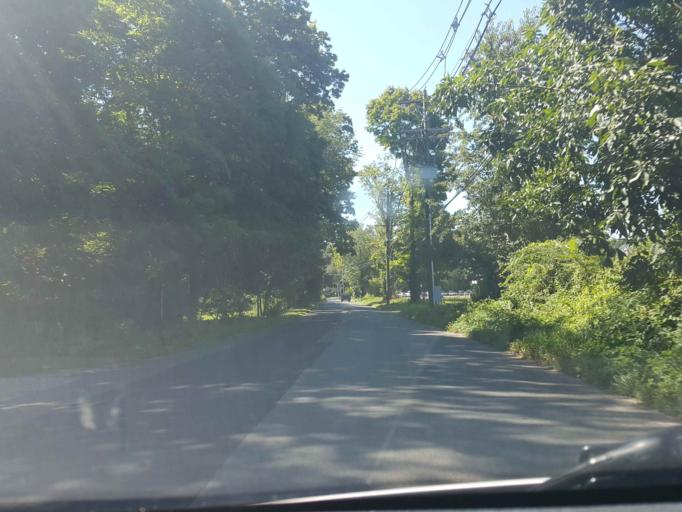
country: US
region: Connecticut
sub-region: New Haven County
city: Guilford
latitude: 41.2921
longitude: -72.6933
